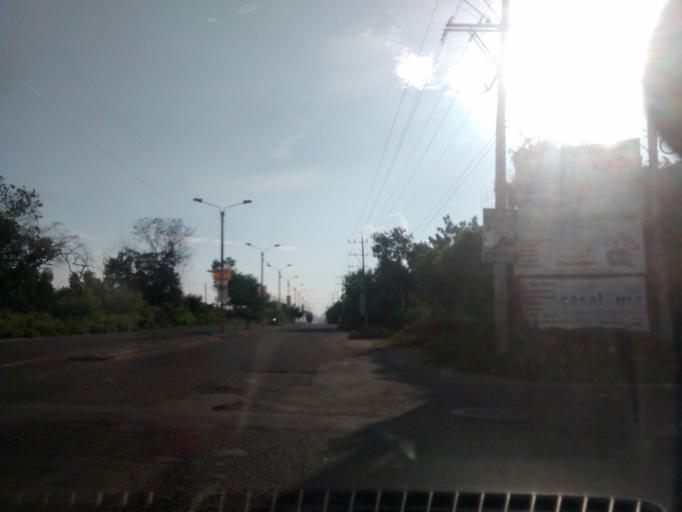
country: CO
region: Cundinamarca
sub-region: Girardot
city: Girardot City
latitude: 4.3017
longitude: -74.8172
